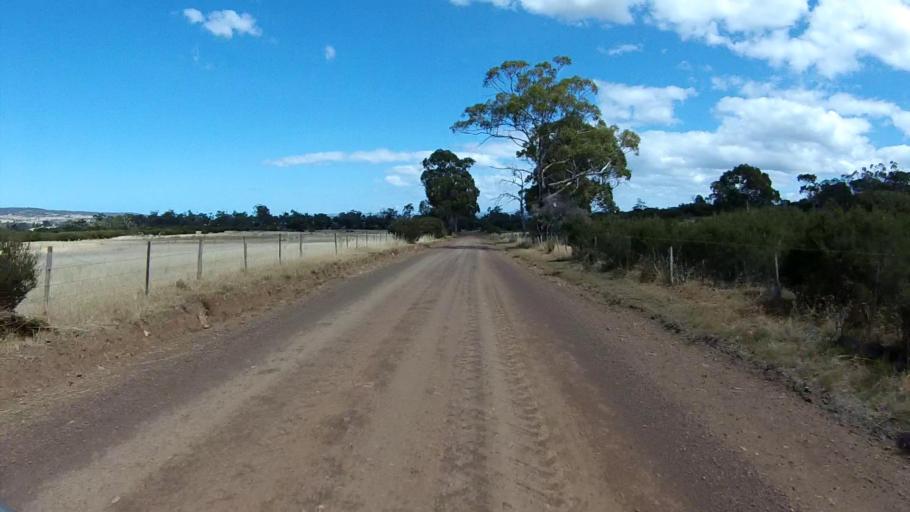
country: AU
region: Tasmania
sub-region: Break O'Day
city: St Helens
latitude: -41.9765
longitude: 148.0706
